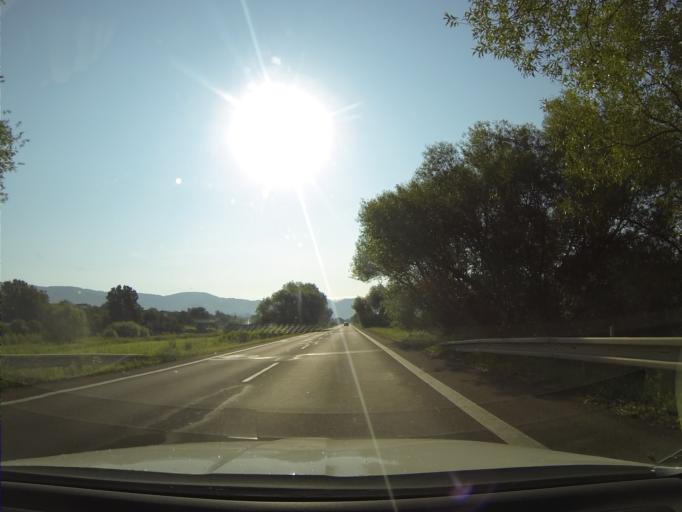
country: SK
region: Nitriansky
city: Handlova
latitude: 48.7785
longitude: 18.7036
